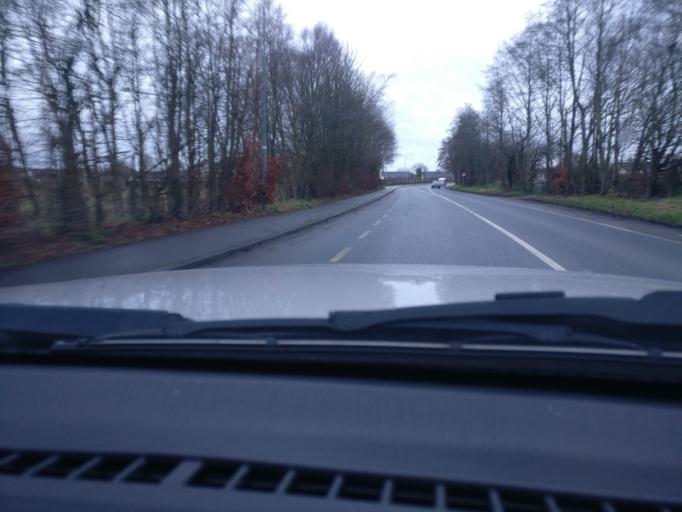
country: IE
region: Leinster
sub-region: An Mhi
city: Trim
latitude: 53.5508
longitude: -6.7871
